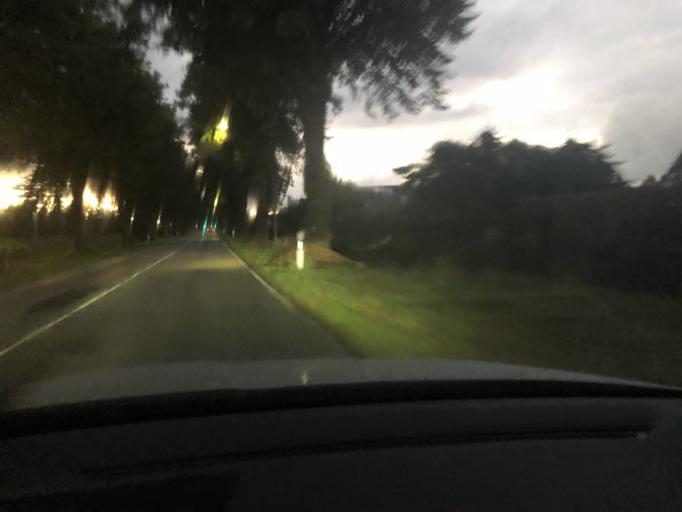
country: DE
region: Schleswig-Holstein
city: Gross Gronau
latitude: 53.8160
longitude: 10.7357
